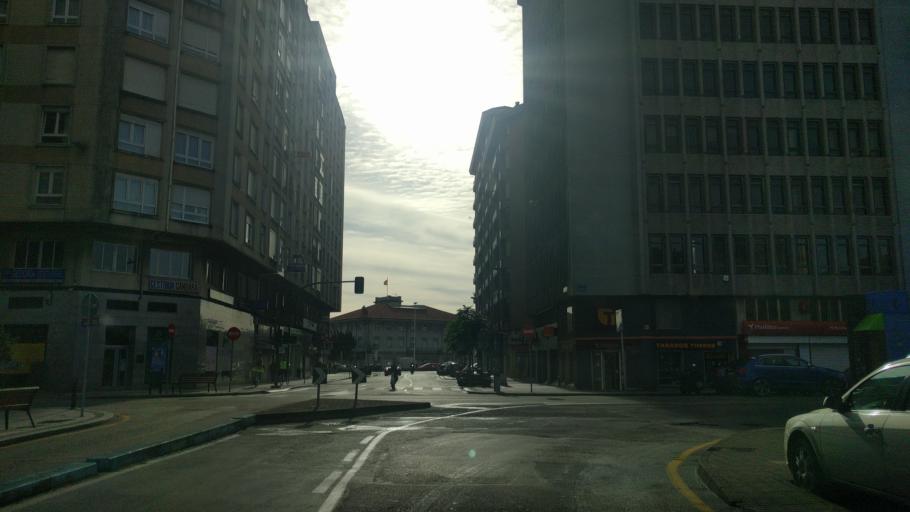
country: ES
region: Cantabria
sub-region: Provincia de Cantabria
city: Santander
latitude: 43.4584
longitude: -3.8103
